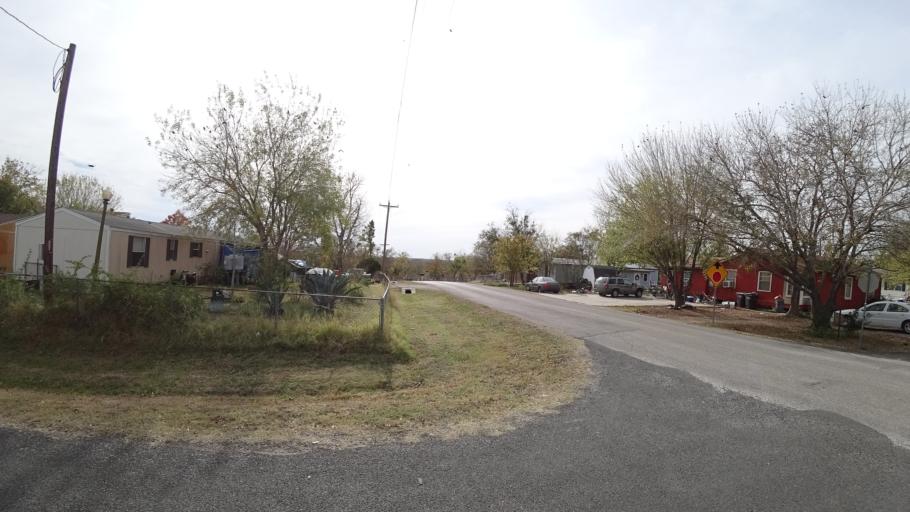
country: US
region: Texas
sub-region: Travis County
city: Garfield
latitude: 30.1295
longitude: -97.6157
